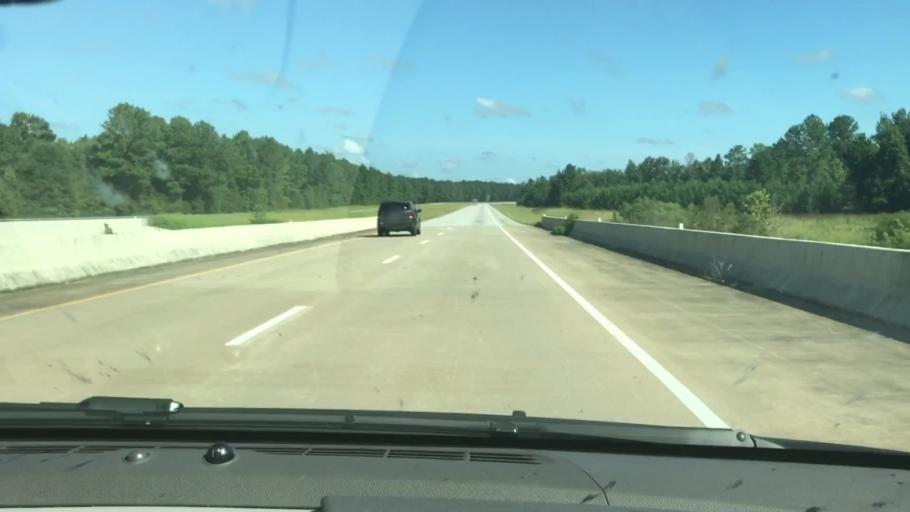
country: US
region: Alabama
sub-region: Barbour County
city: Eufaula
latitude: 32.1816
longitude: -85.1793
